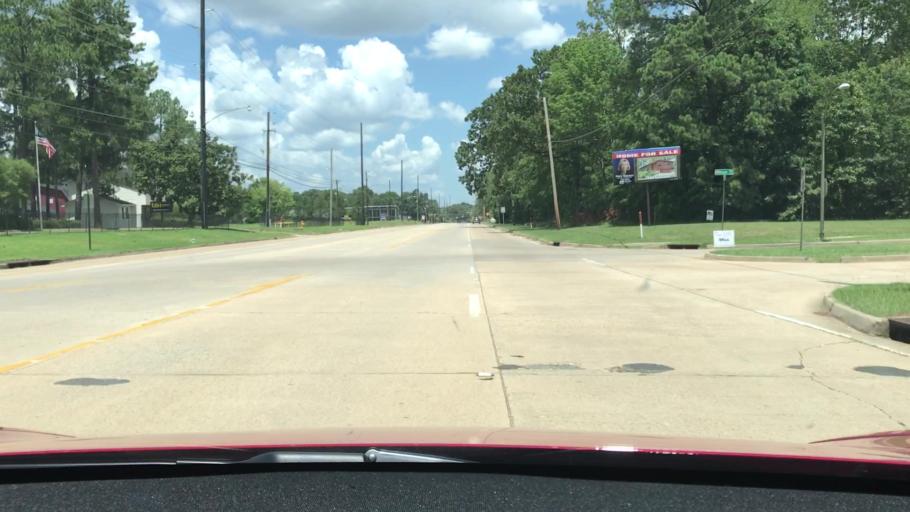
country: US
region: Louisiana
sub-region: Bossier Parish
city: Bossier City
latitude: 32.4251
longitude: -93.7396
